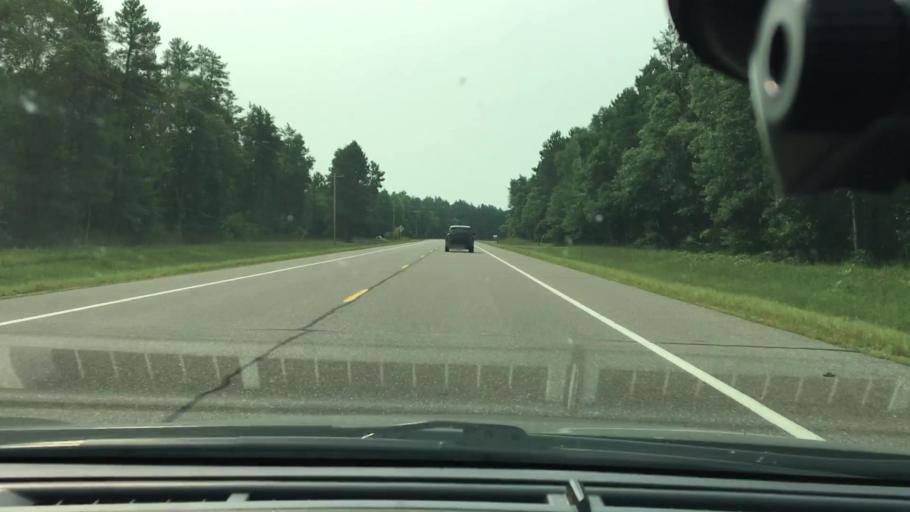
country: US
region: Minnesota
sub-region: Crow Wing County
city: Cross Lake
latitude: 46.5707
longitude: -94.1292
